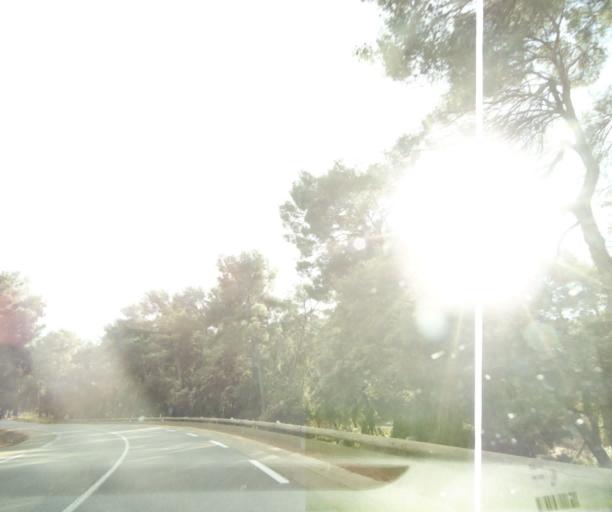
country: FR
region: Provence-Alpes-Cote d'Azur
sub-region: Departement des Bouches-du-Rhone
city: Sausset-les-Pins
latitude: 43.3570
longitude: 5.1022
